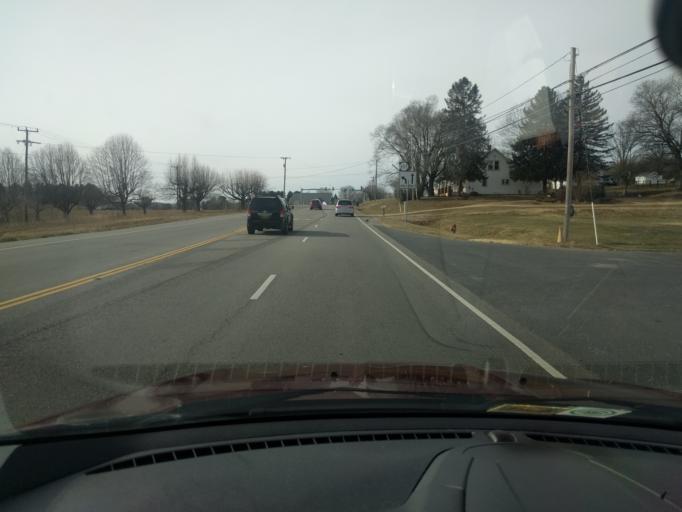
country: US
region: Virginia
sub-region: Augusta County
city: Stuarts Draft
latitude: 38.0303
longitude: -79.0517
